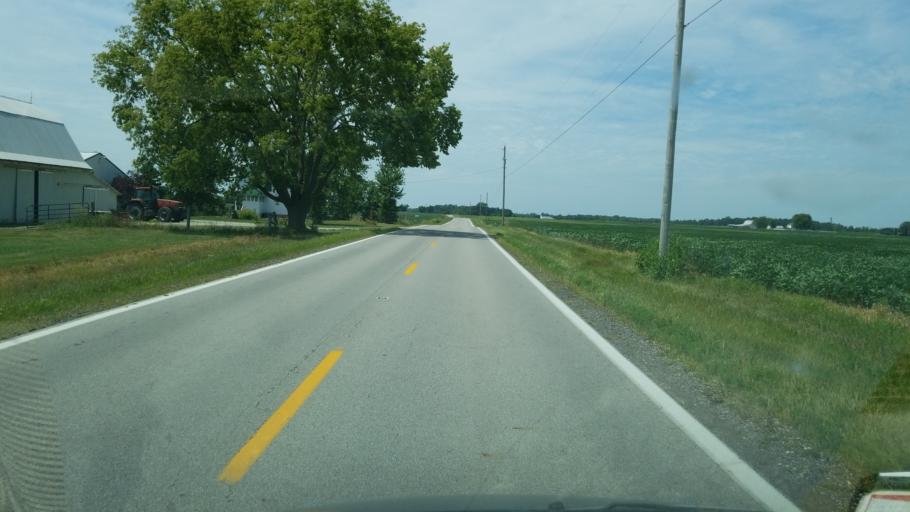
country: US
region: Ohio
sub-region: Madison County
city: West Jefferson
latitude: 39.8768
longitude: -83.3163
